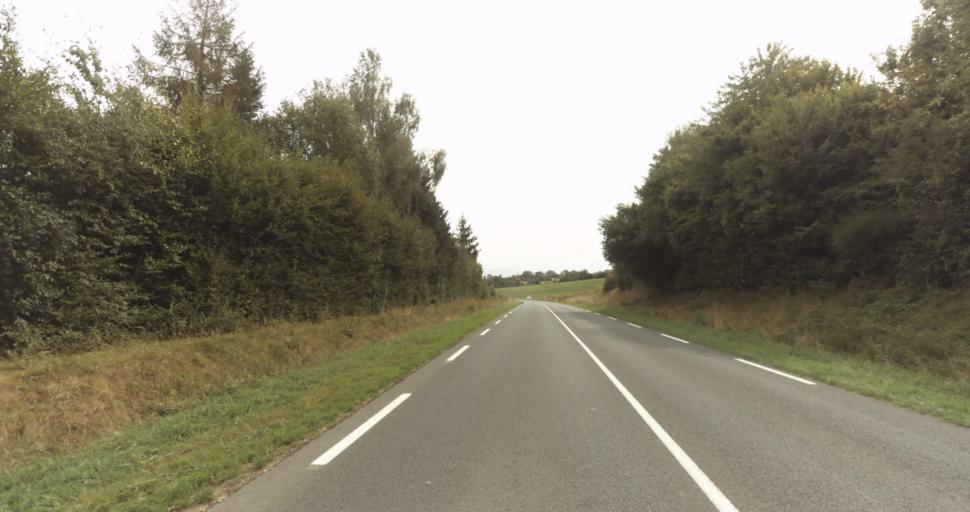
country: FR
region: Lower Normandy
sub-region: Departement de l'Orne
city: Gace
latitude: 48.8150
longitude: 0.2805
